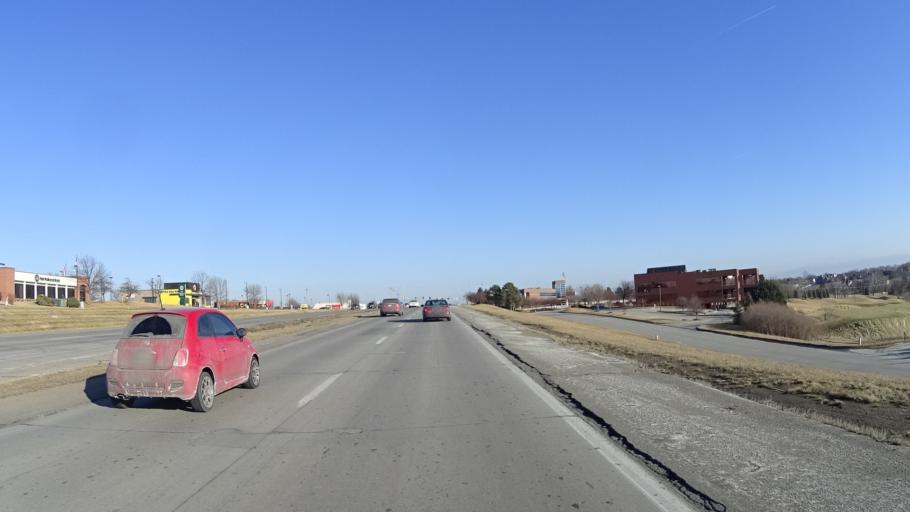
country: US
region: Nebraska
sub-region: Douglas County
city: Bennington
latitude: 41.2921
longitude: -96.1237
